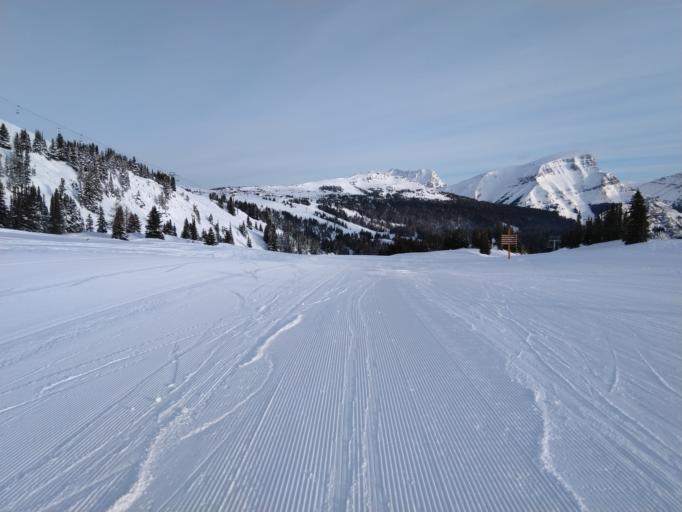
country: CA
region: Alberta
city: Banff
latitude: 51.0713
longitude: -115.7824
